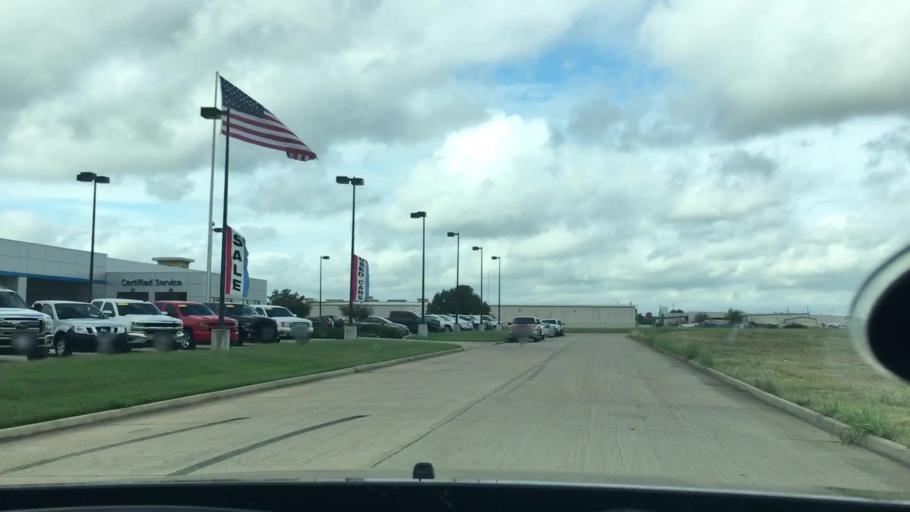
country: US
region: Oklahoma
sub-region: Bryan County
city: Durant
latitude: 34.0029
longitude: -96.4033
